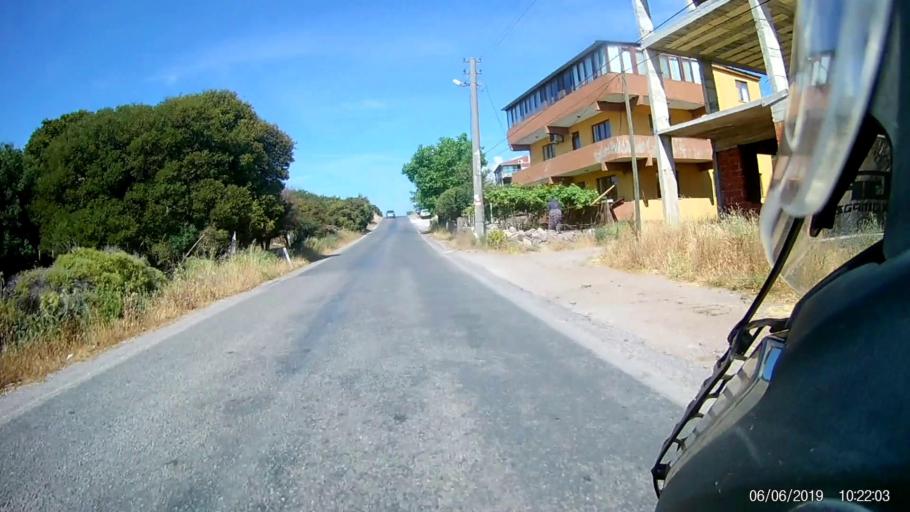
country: TR
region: Canakkale
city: Ayvacik
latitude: 39.5135
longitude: 26.4350
